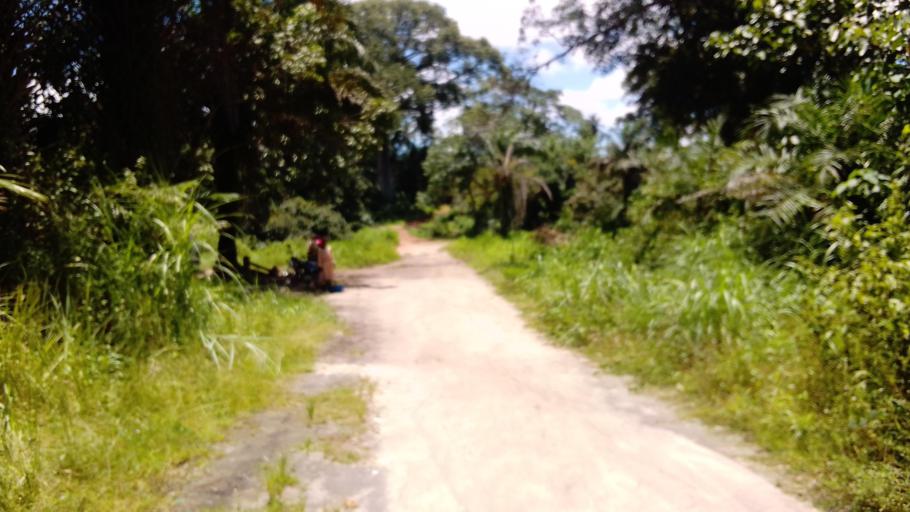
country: SL
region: Northern Province
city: Makeni
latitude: 9.0358
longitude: -12.1592
